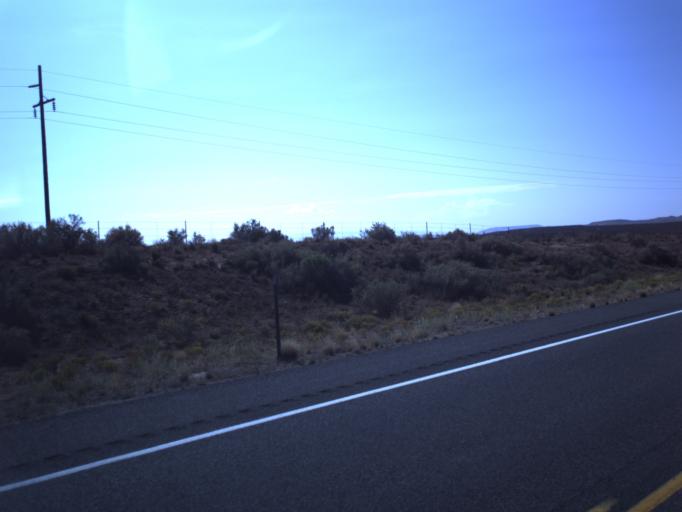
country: US
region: Utah
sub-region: San Juan County
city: Blanding
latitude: 37.3856
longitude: -109.5009
